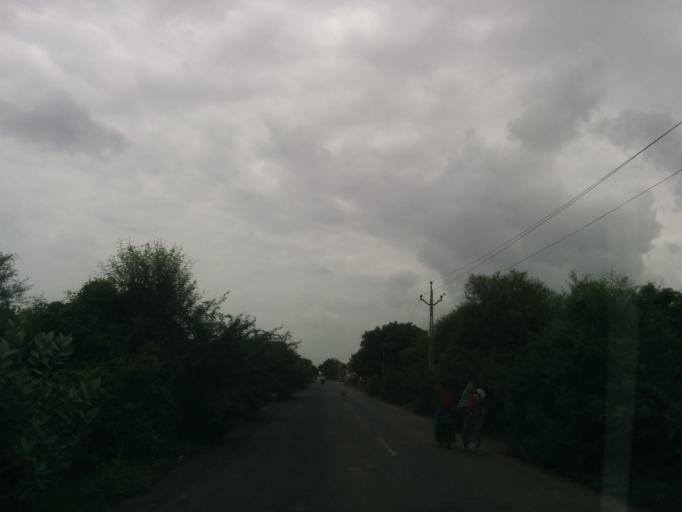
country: IN
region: Gujarat
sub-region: Ahmadabad
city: Sanand
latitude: 23.0659
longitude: 72.3918
